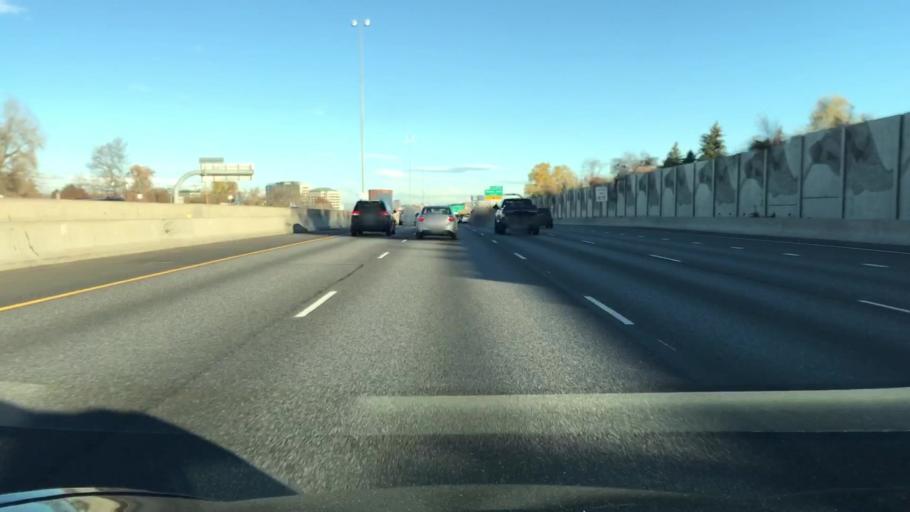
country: US
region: Colorado
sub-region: Arapahoe County
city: Glendale
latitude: 39.6711
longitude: -104.9279
